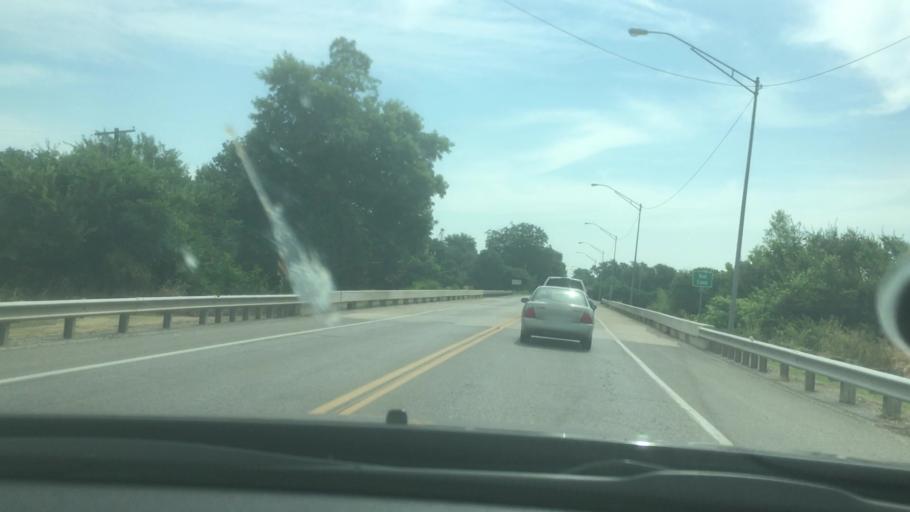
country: US
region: Oklahoma
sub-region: Garvin County
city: Maysville
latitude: 34.8172
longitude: -97.4142
